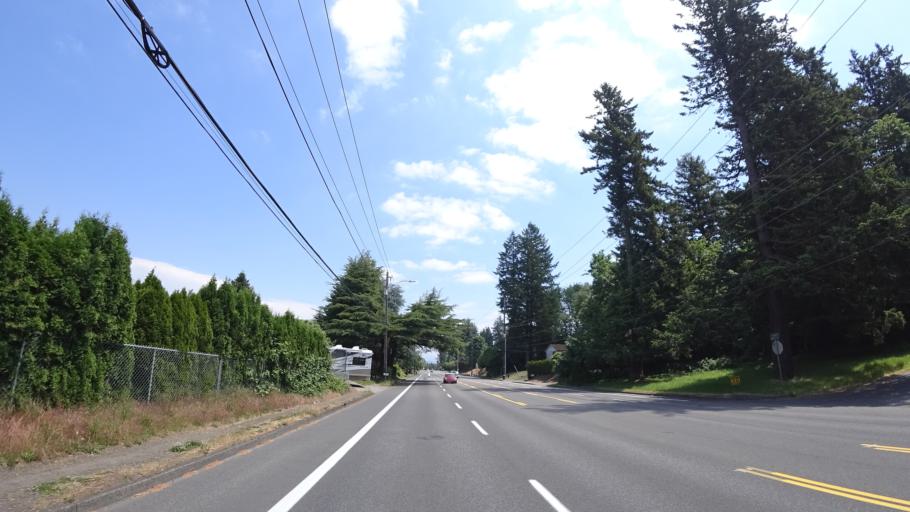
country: US
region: Oregon
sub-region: Multnomah County
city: Fairview
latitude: 45.5337
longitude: -122.5036
